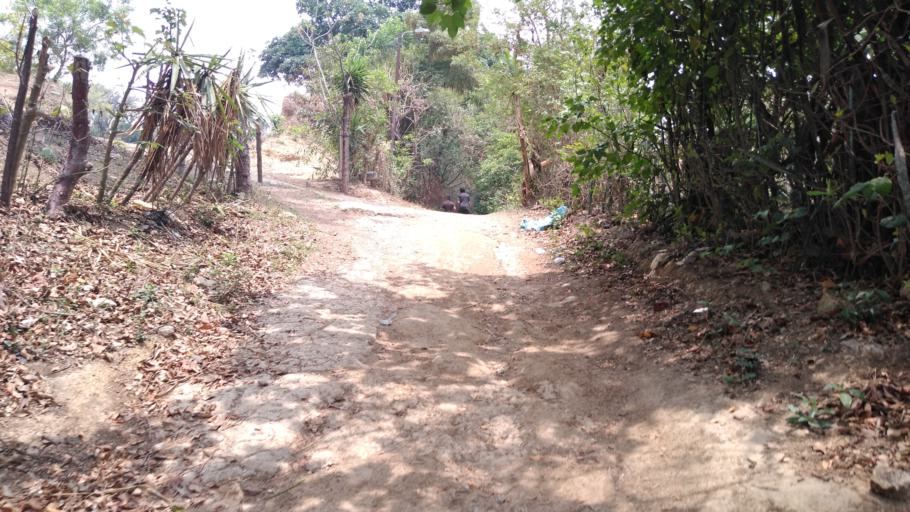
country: GT
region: Guatemala
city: Petapa
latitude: 14.5062
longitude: -90.5557
